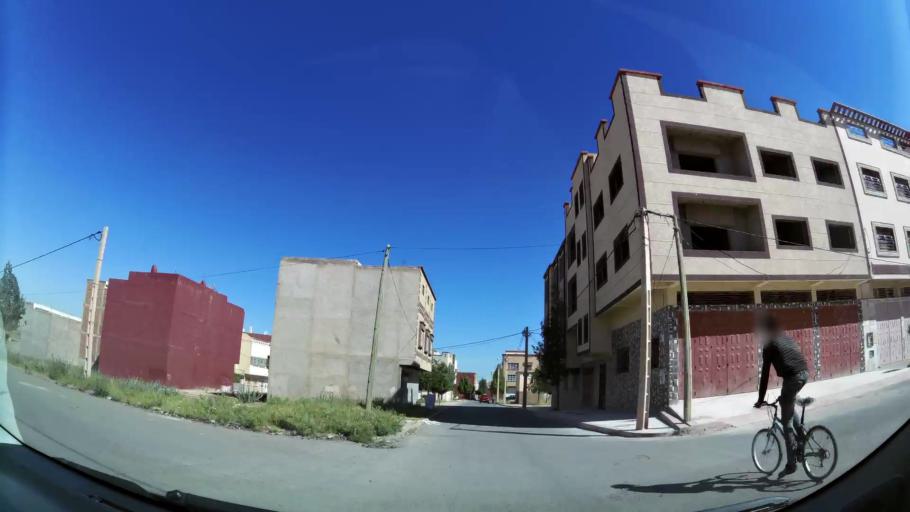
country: MA
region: Oriental
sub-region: Oujda-Angad
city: Oujda
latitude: 34.6498
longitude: -1.8850
